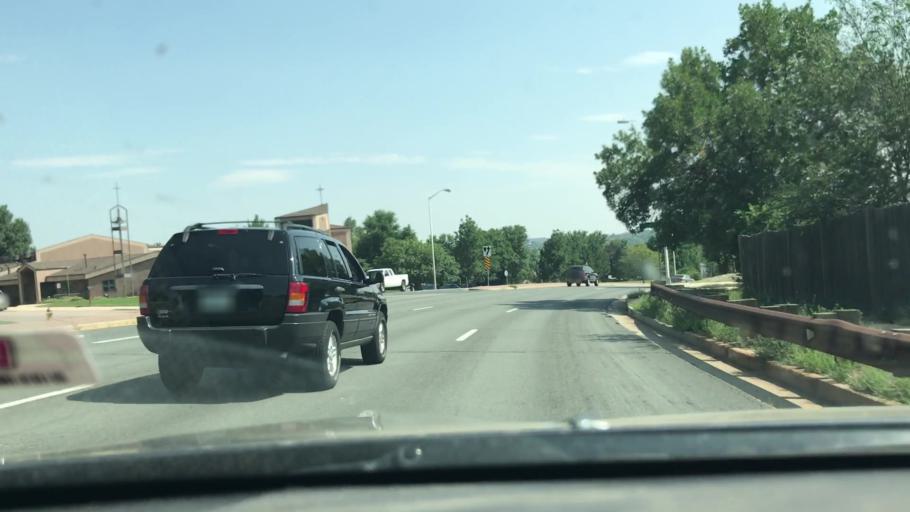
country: US
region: Colorado
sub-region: El Paso County
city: Colorado Springs
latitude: 38.9085
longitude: -104.7749
